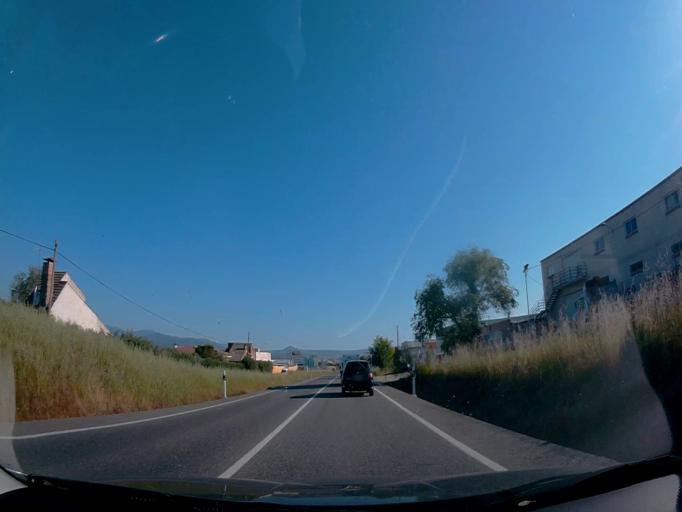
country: ES
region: Castille-La Mancha
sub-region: Province of Toledo
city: Escalona
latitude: 40.1310
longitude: -4.4050
